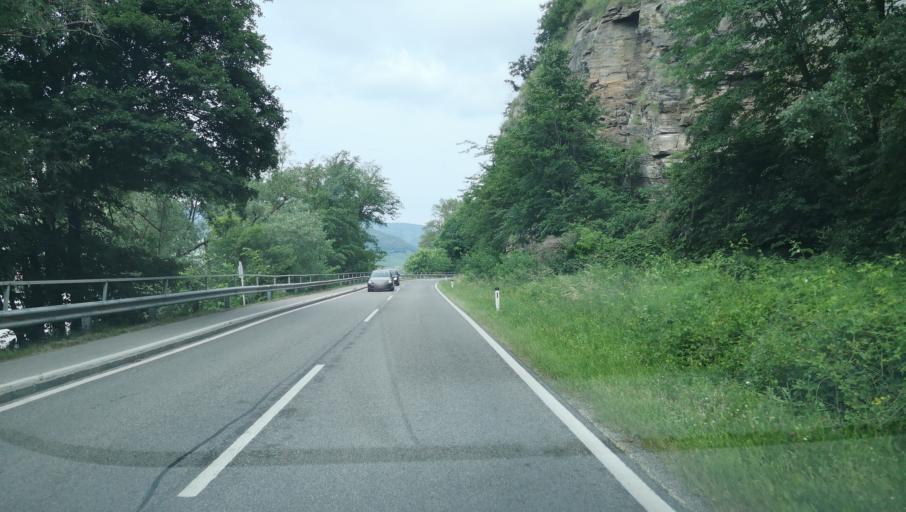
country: AT
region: Lower Austria
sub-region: Politischer Bezirk Krems
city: Spitz
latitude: 48.3761
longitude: 15.4552
